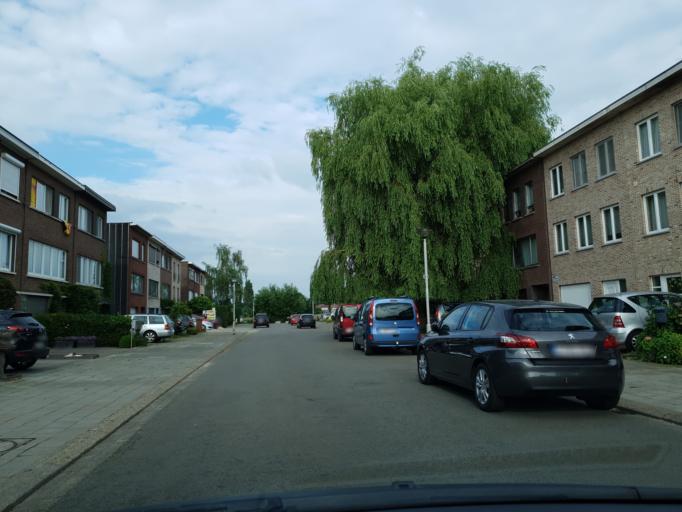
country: BE
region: Flanders
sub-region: Provincie Antwerpen
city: Kapellen
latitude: 51.2751
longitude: 4.4427
